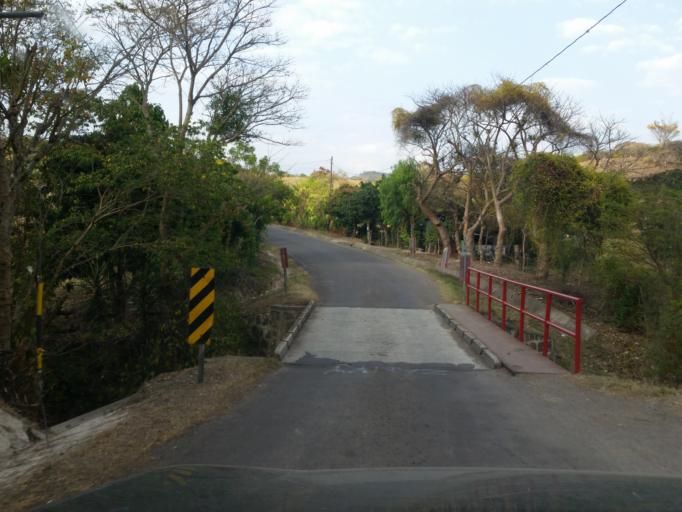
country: NI
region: Jinotega
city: San Rafael del Norte
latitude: 13.1938
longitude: -86.1197
